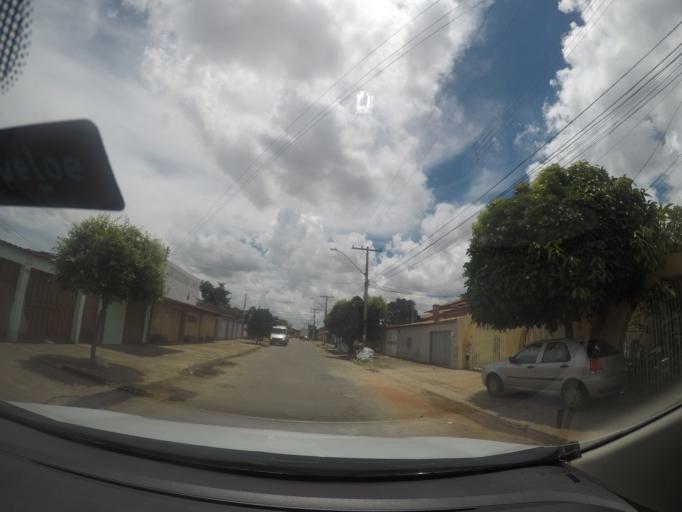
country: BR
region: Goias
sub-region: Goiania
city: Goiania
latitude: -16.6739
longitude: -49.3091
